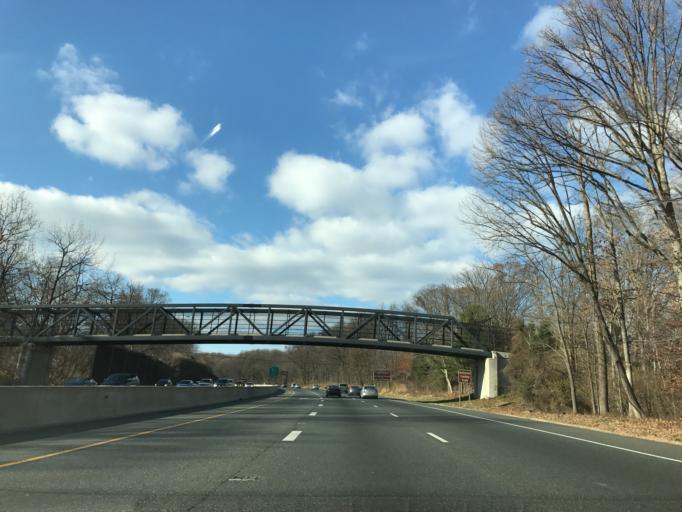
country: US
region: Maryland
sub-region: Montgomery County
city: North Bethesda
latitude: 39.0269
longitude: -77.1107
